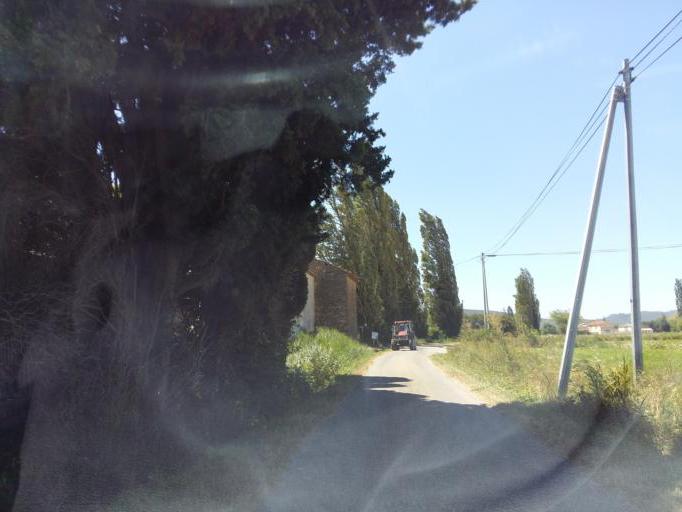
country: FR
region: Provence-Alpes-Cote d'Azur
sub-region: Departement du Vaucluse
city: Piolenc
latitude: 44.1541
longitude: 4.7597
